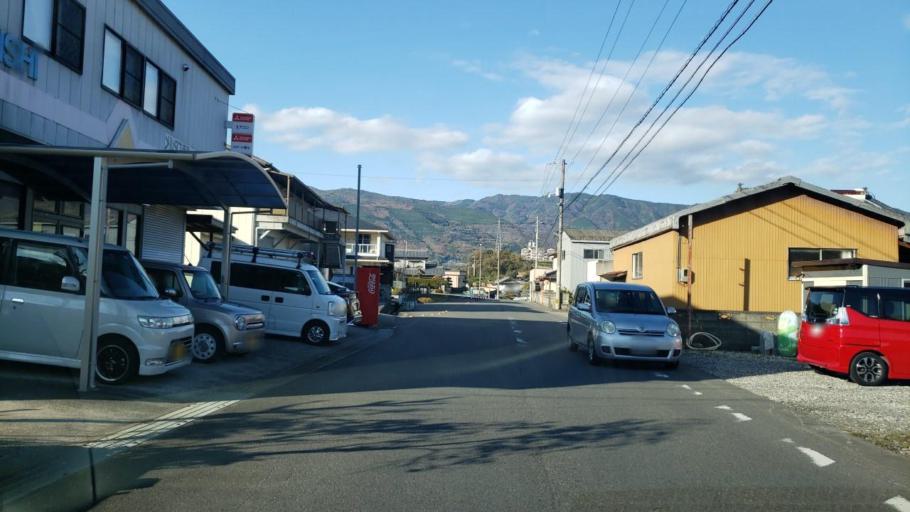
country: JP
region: Tokushima
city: Wakimachi
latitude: 34.0328
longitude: 134.0293
